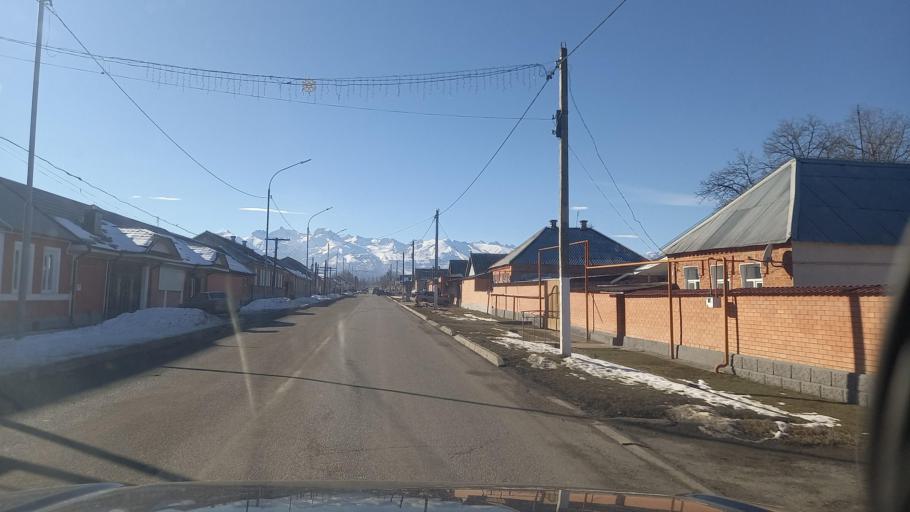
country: RU
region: North Ossetia
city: Chikola
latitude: 43.1948
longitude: 43.9158
